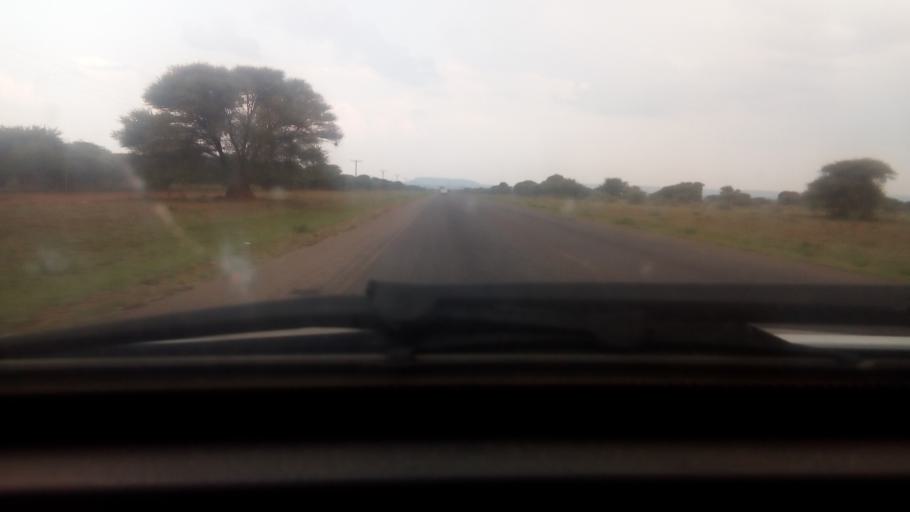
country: BW
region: Kweneng
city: Metsemotlhaba
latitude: -24.5165
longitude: 25.7612
